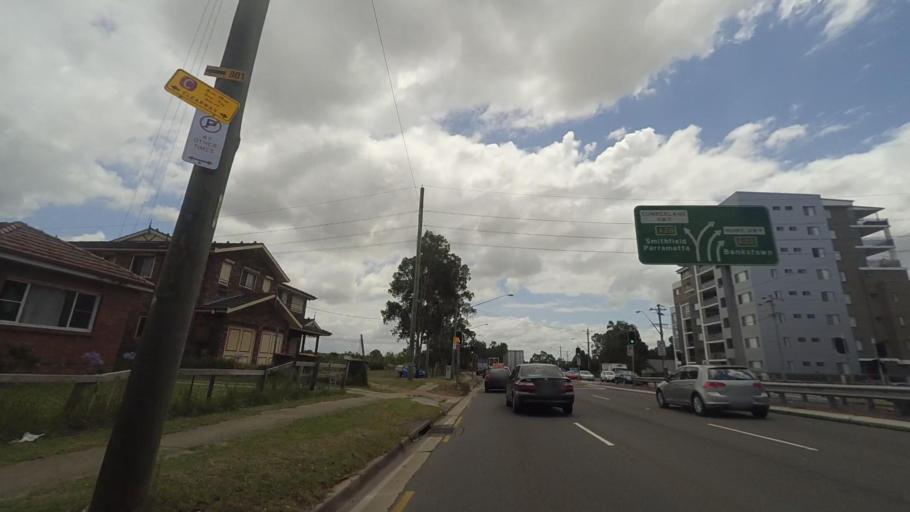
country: AU
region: New South Wales
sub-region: Fairfield
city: Liverpool
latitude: -33.9176
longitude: 150.9197
